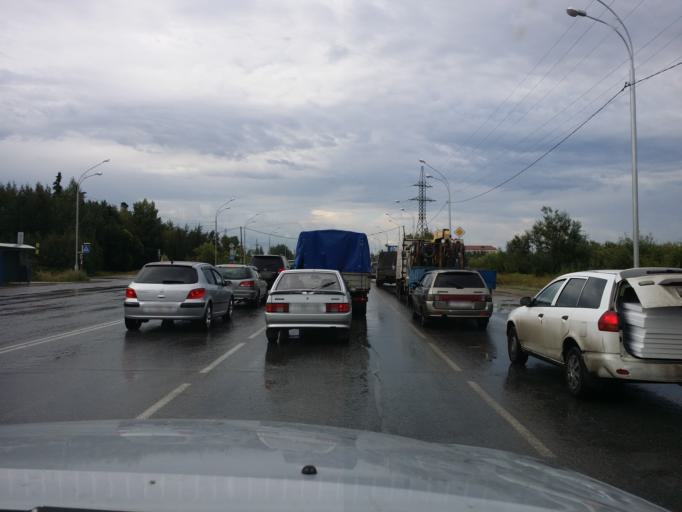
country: RU
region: Khanty-Mansiyskiy Avtonomnyy Okrug
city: Nizhnevartovsk
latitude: 60.9547
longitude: 76.5302
